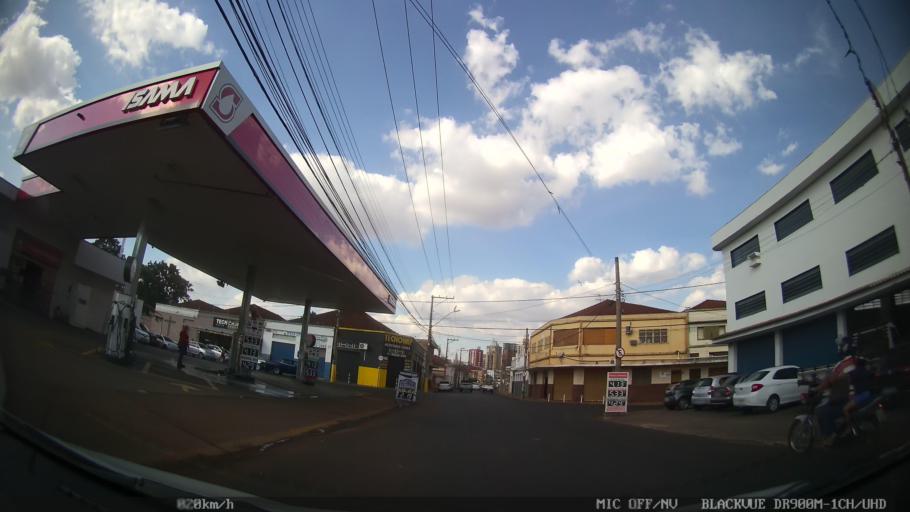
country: BR
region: Sao Paulo
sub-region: Ribeirao Preto
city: Ribeirao Preto
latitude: -21.1782
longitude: -47.8210
